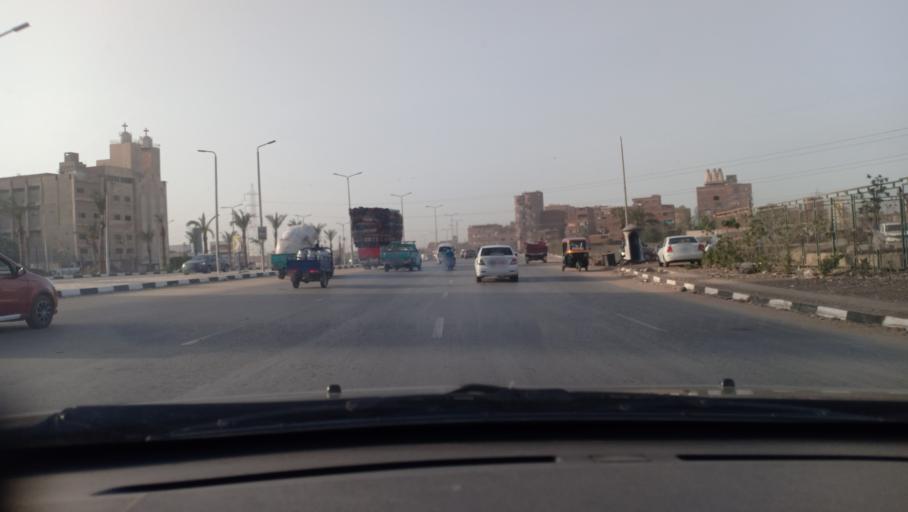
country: EG
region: Muhafazat al Qalyubiyah
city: Qalyub
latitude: 30.1386
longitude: 31.2643
